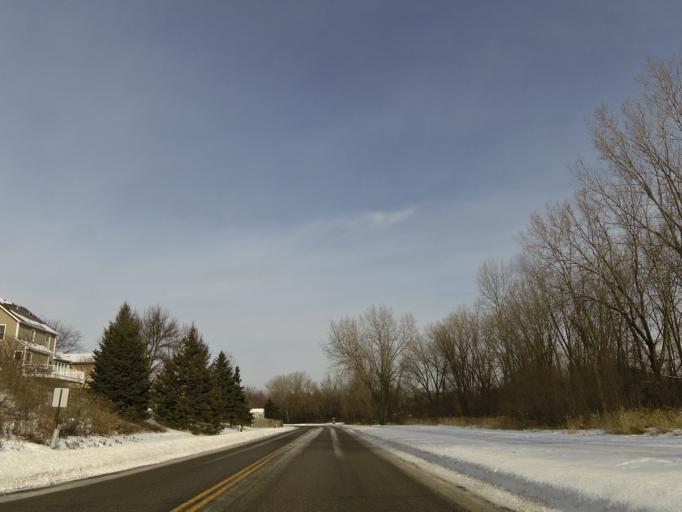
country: US
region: Minnesota
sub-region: Carver County
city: Chanhassen
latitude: 44.8814
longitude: -93.5113
